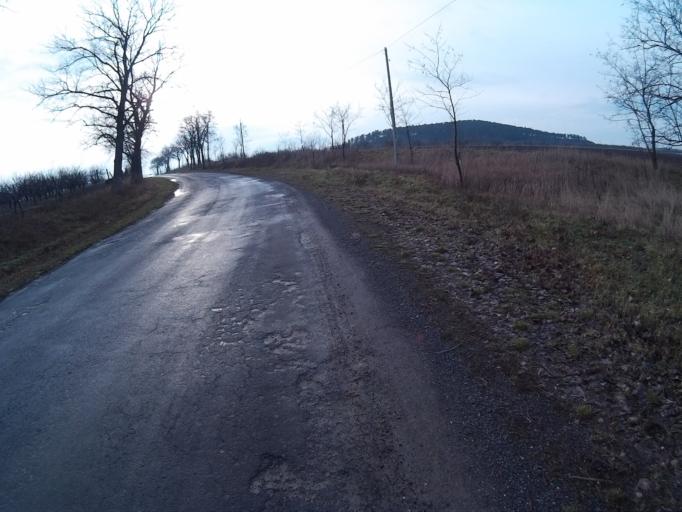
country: HU
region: Borsod-Abauj-Zemplen
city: Abaujszanto
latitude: 48.3430
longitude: 21.2153
